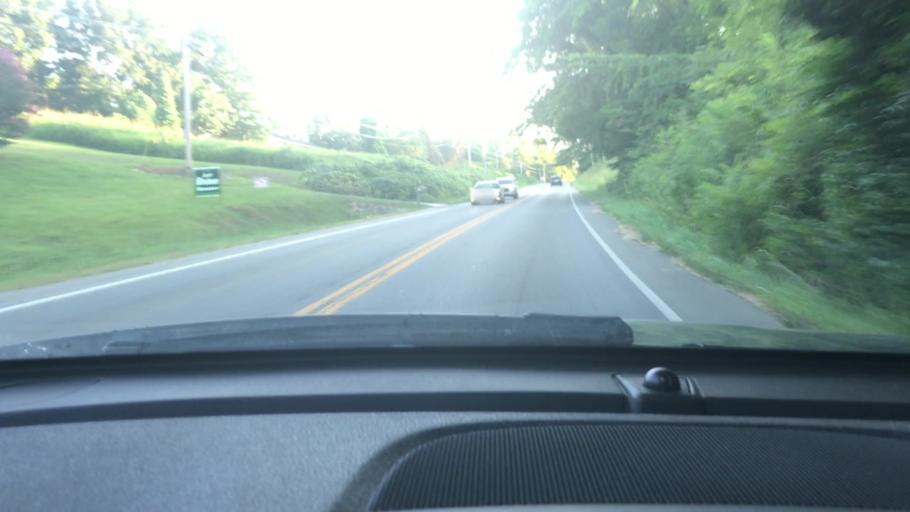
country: US
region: Tennessee
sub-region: Dickson County
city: Charlotte
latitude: 36.1742
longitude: -87.3433
